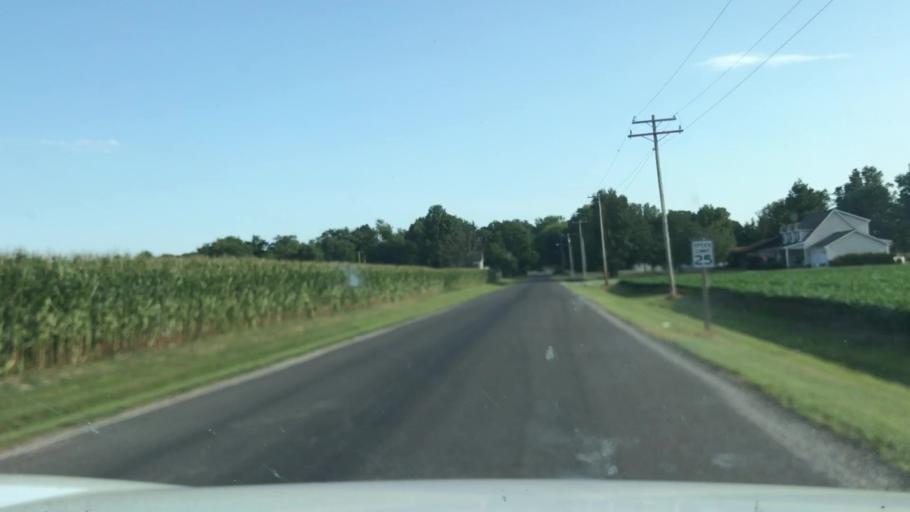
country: US
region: Illinois
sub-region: Washington County
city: Okawville
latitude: 38.3970
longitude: -89.4866
